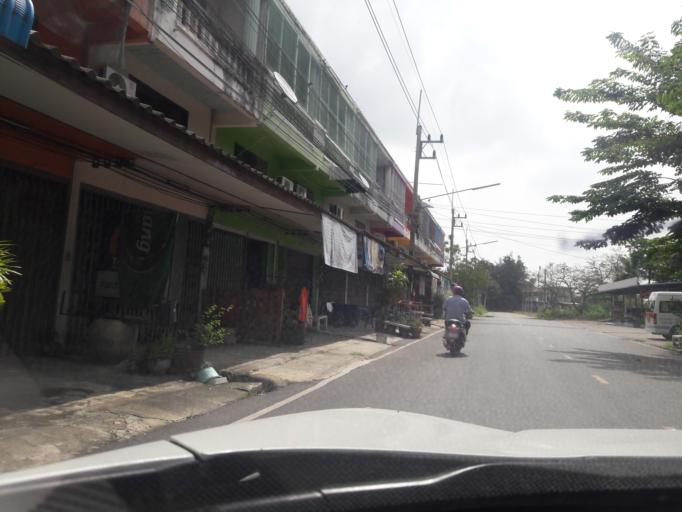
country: TH
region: Lop Buri
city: Ban Mi
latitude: 15.0401
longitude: 100.5425
